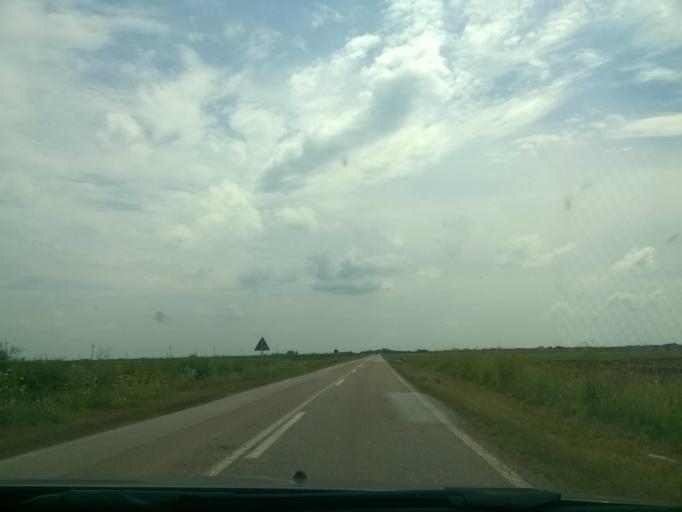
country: RS
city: Hajducica
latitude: 45.2498
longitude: 20.9768
